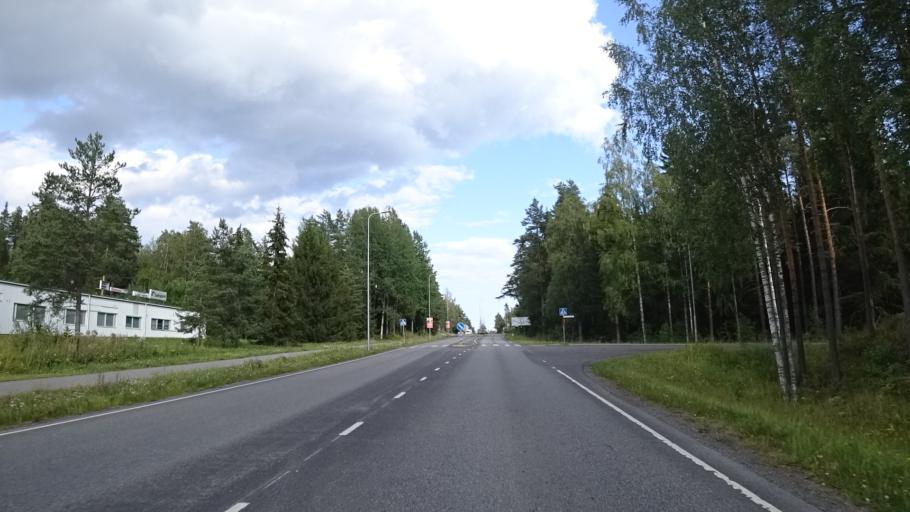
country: FI
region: South Karelia
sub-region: Imatra
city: Imatra
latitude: 61.1726
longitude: 28.7412
